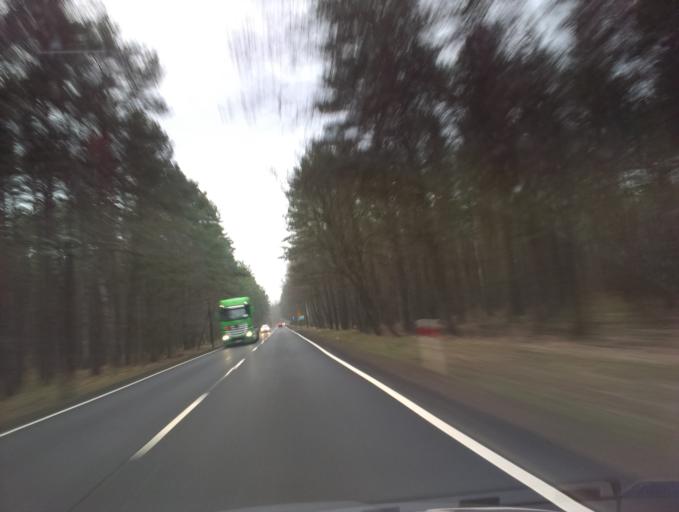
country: PL
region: Greater Poland Voivodeship
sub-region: Powiat zlotowski
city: Tarnowka
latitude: 53.2897
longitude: 16.7822
